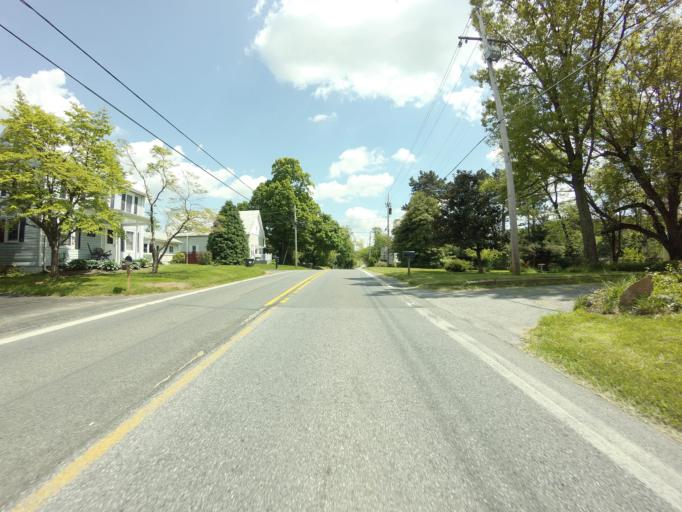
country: US
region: Maryland
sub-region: Montgomery County
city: Damascus
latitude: 39.3389
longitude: -77.2310
